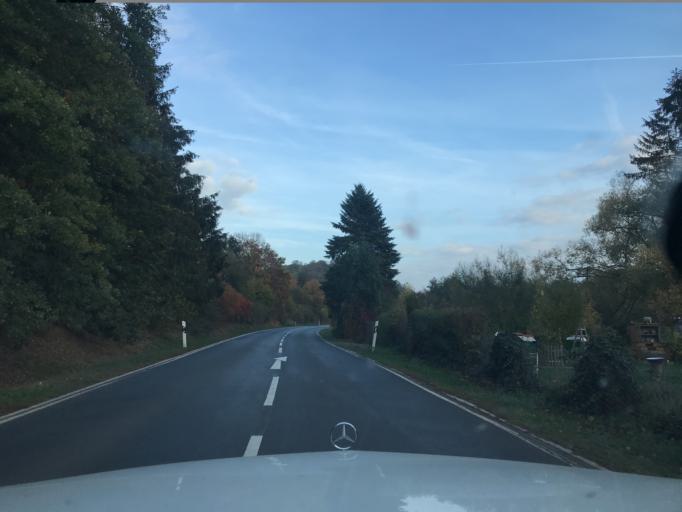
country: DE
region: Hesse
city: Grebenstein
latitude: 51.4412
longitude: 9.4032
